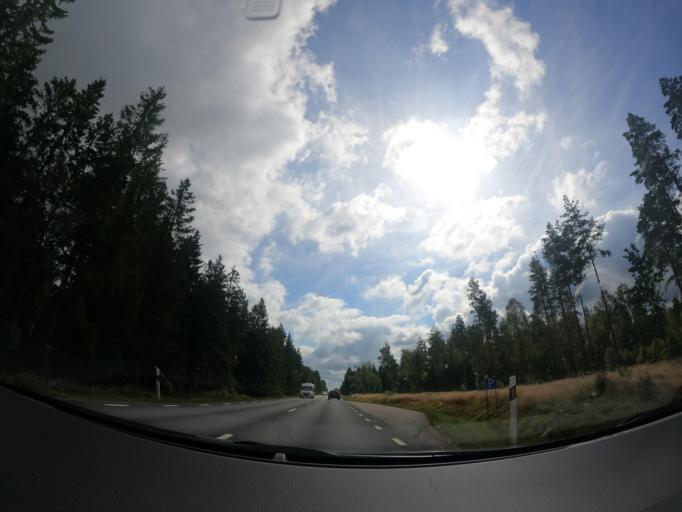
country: SE
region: Joenkoeping
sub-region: Gislaveds Kommun
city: Smalandsstenar
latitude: 57.1243
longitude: 13.3461
